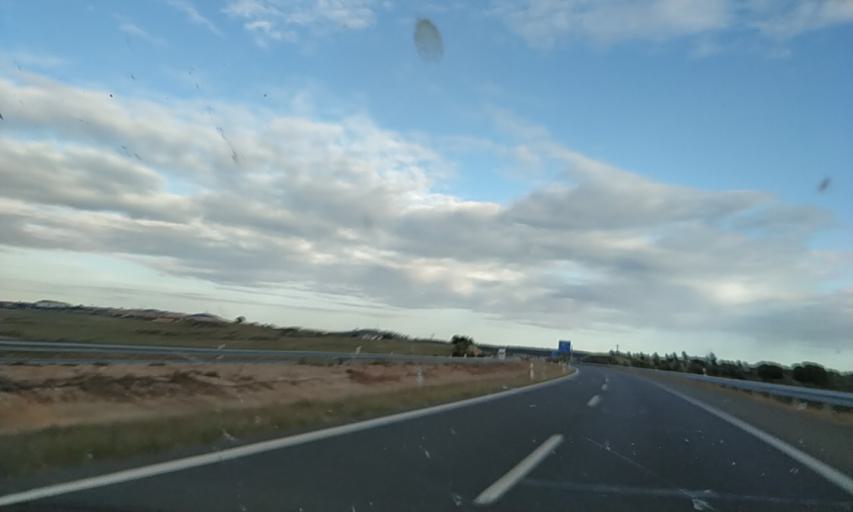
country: ES
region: Extremadura
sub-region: Provincia de Caceres
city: Caceres
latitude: 39.4775
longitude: -6.4333
